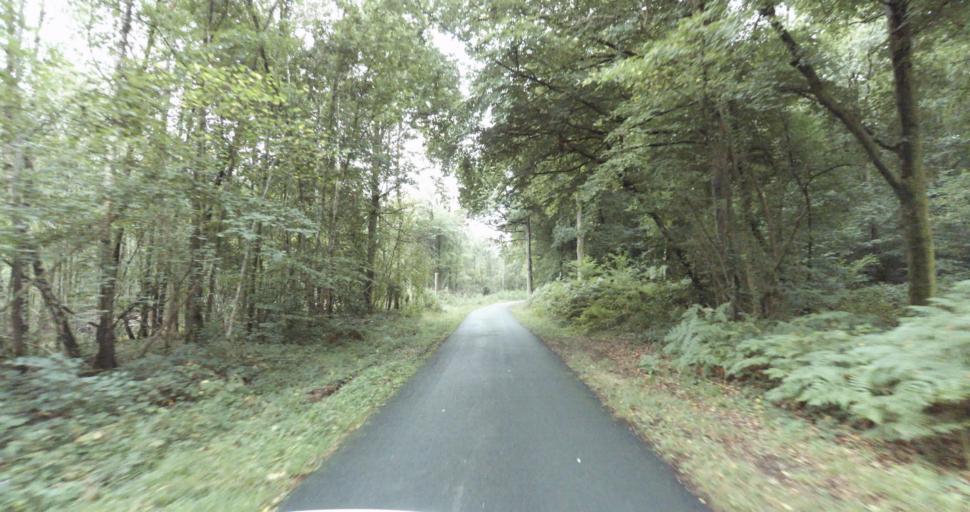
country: FR
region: Lower Normandy
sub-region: Departement de l'Orne
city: Vimoutiers
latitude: 48.9034
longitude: 0.1133
